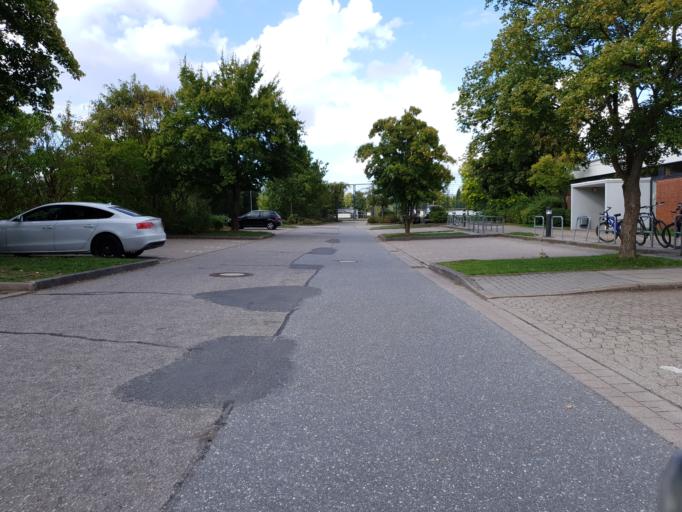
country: DE
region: Schleswig-Holstein
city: Kronshagen
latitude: 54.3407
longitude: 10.0812
